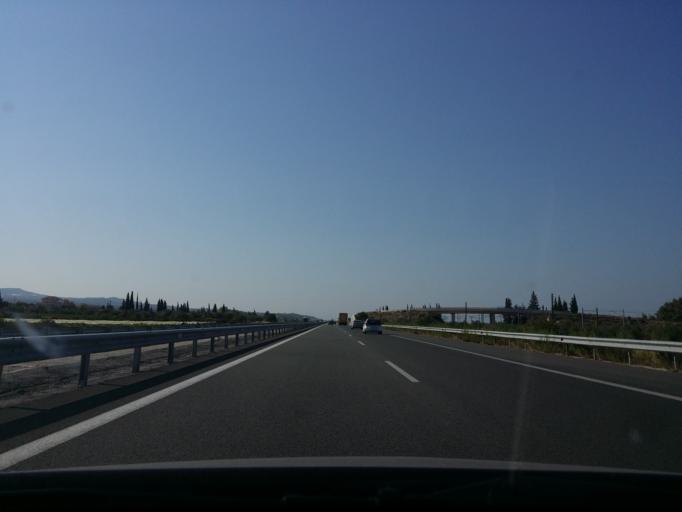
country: GR
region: Peloponnese
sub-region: Nomos Korinthias
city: Velo
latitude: 37.9500
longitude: 22.7560
